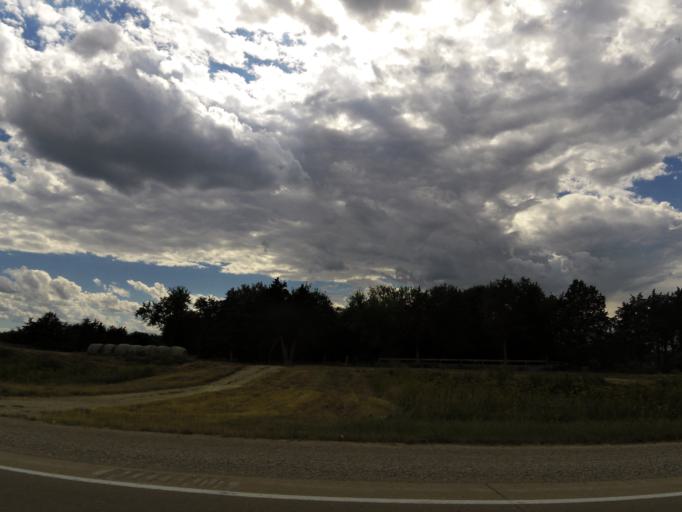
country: US
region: Iowa
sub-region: Henry County
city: Mount Pleasant
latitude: 40.8328
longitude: -91.5649
